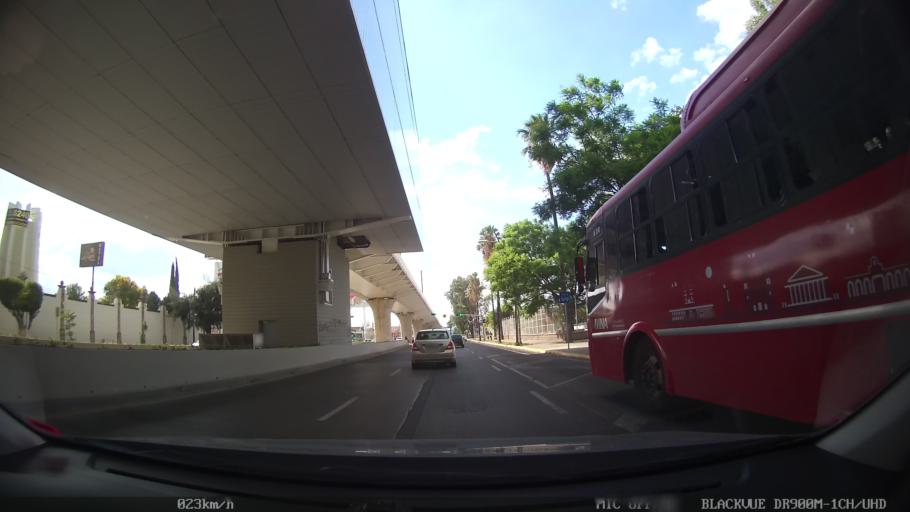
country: MX
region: Jalisco
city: Tlaquepaque
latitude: 20.6316
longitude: -103.2956
